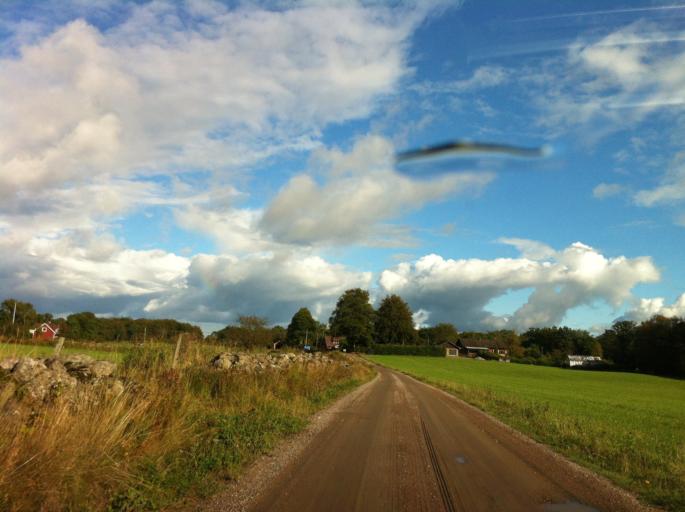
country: SE
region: Skane
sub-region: Hassleholms Kommun
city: Sosdala
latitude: 56.1221
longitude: 13.5990
